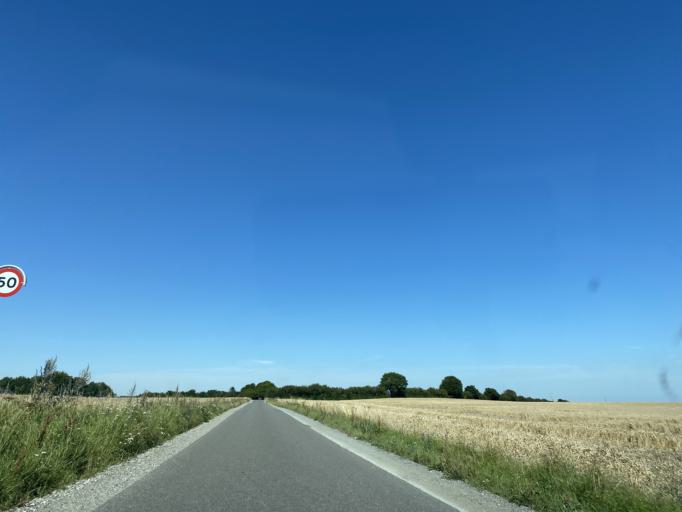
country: DK
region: South Denmark
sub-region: Kolding Kommune
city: Kolding
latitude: 55.5209
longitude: 9.5121
